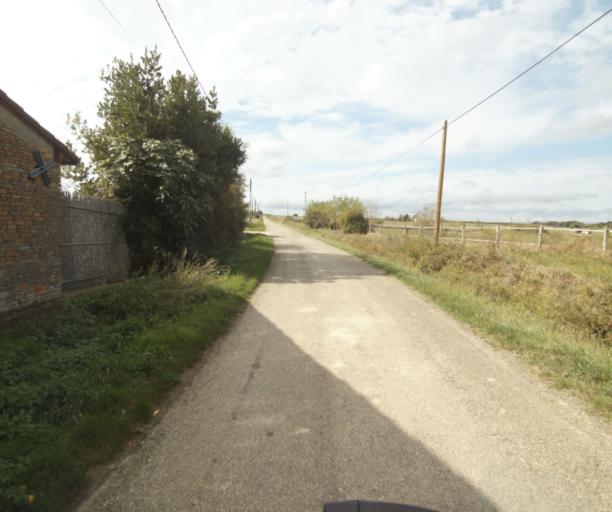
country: FR
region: Midi-Pyrenees
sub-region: Departement du Tarn-et-Garonne
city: Verdun-sur-Garonne
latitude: 43.8623
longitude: 1.1706
